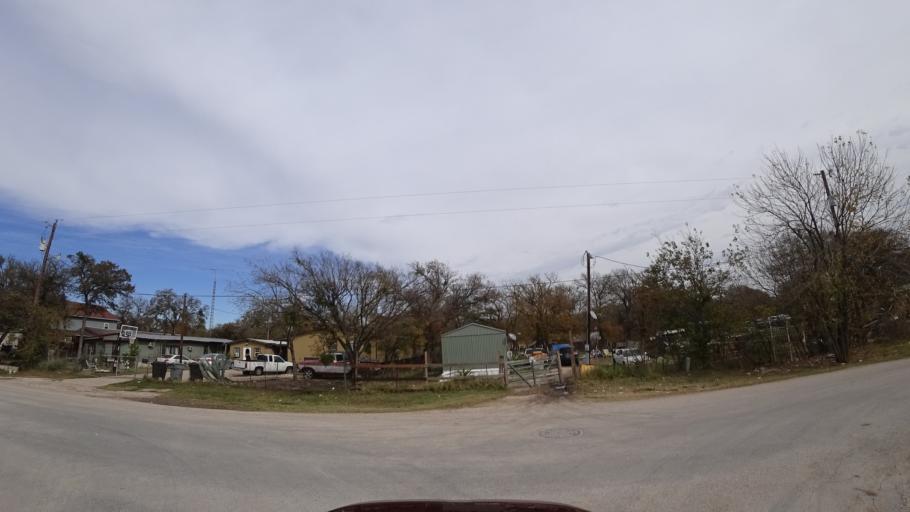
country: US
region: Texas
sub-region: Travis County
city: Garfield
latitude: 30.1319
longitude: -97.5681
